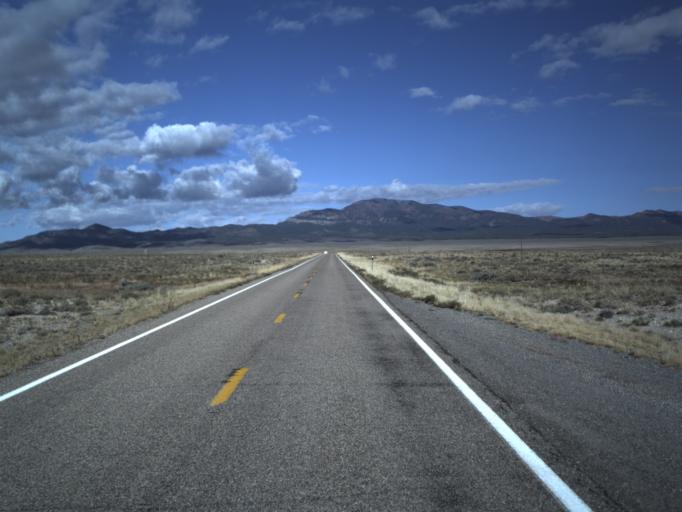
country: US
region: Utah
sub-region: Beaver County
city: Milford
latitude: 38.4276
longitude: -113.1211
